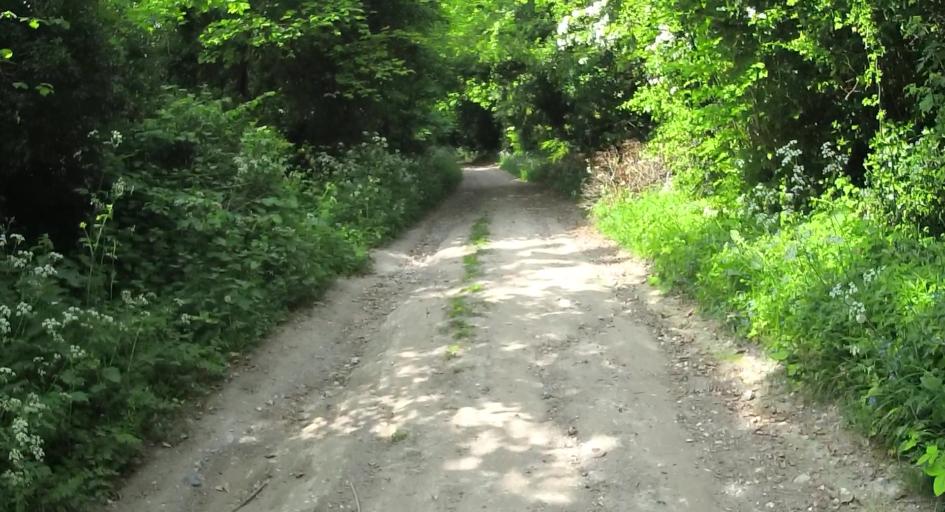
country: GB
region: England
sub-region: Hampshire
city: Kingsclere
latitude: 51.3225
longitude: -1.2395
